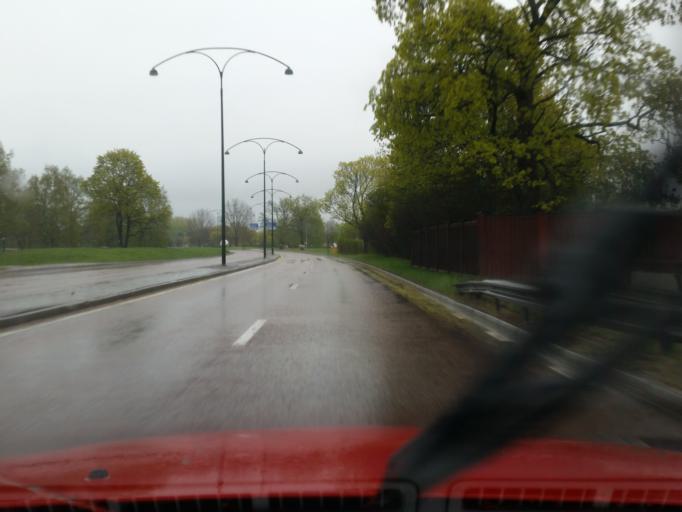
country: SE
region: Dalarna
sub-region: Borlange Kommun
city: Borlaenge
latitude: 60.4971
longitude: 15.3993
